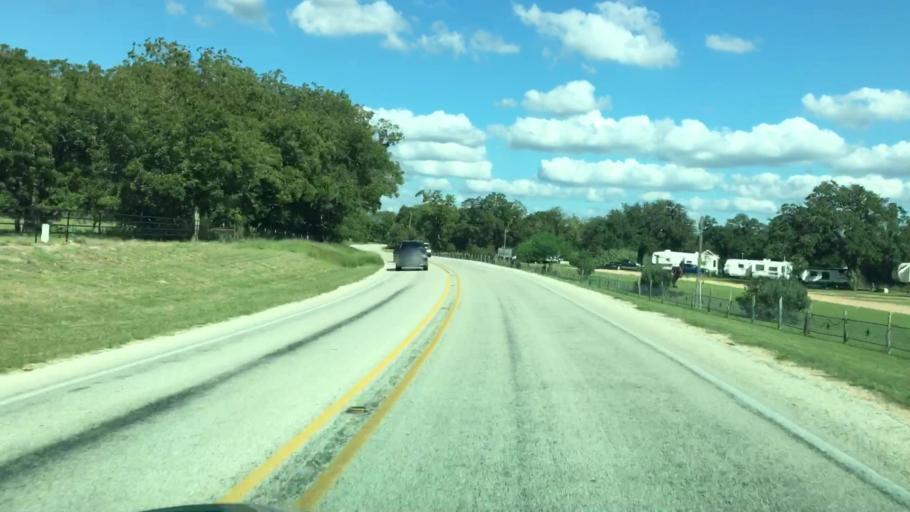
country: US
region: Texas
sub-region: Blanco County
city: Blanco
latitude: 30.0912
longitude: -98.3979
